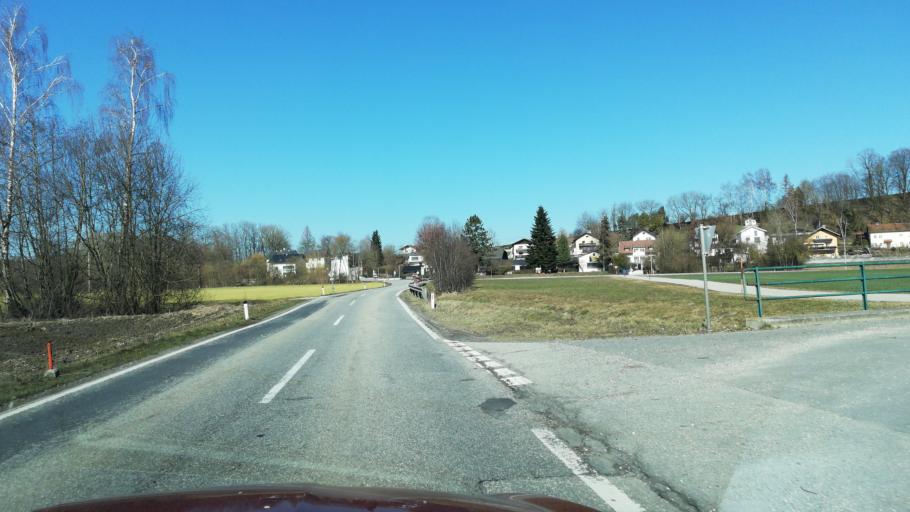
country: AT
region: Upper Austria
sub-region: Politischer Bezirk Vocklabruck
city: Schwanenstadt
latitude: 48.0611
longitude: 13.7681
